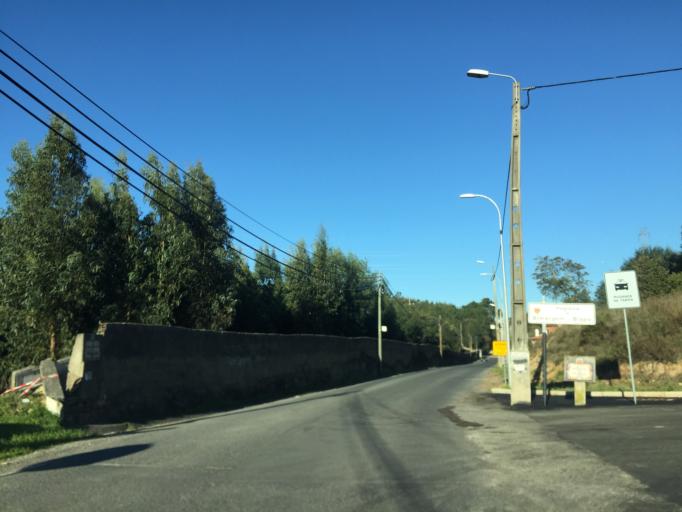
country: PT
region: Lisbon
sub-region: Odivelas
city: Canecas
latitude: 38.8190
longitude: -9.2335
